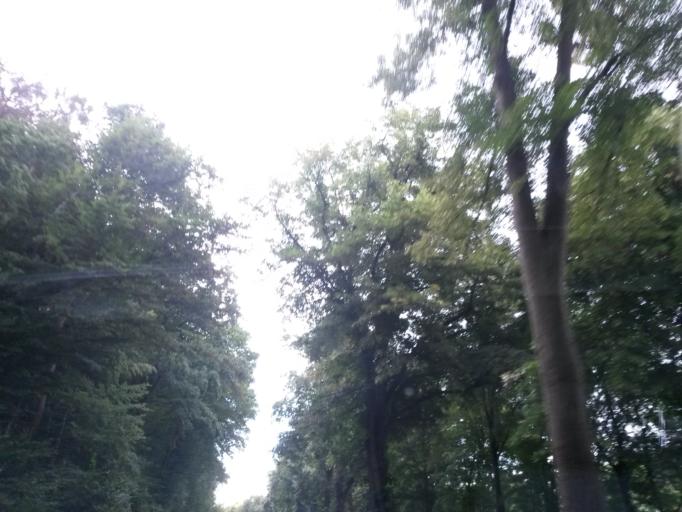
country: DE
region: North Rhine-Westphalia
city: Lohmar
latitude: 50.8655
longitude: 7.2079
